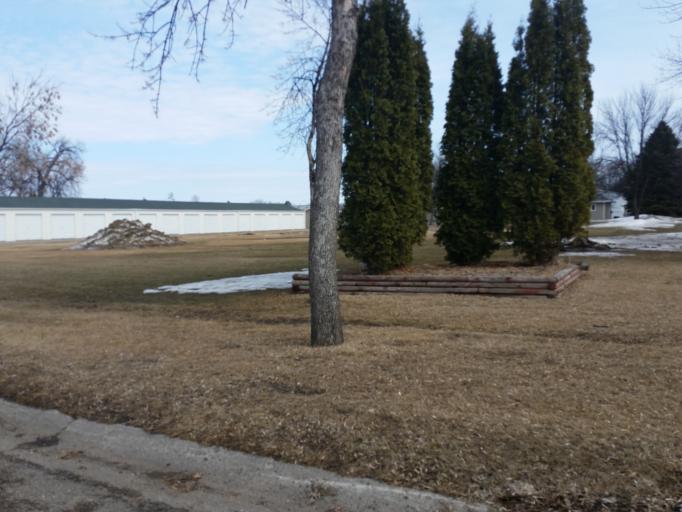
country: US
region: North Dakota
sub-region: Walsh County
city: Grafton
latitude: 48.4110
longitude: -97.4235
